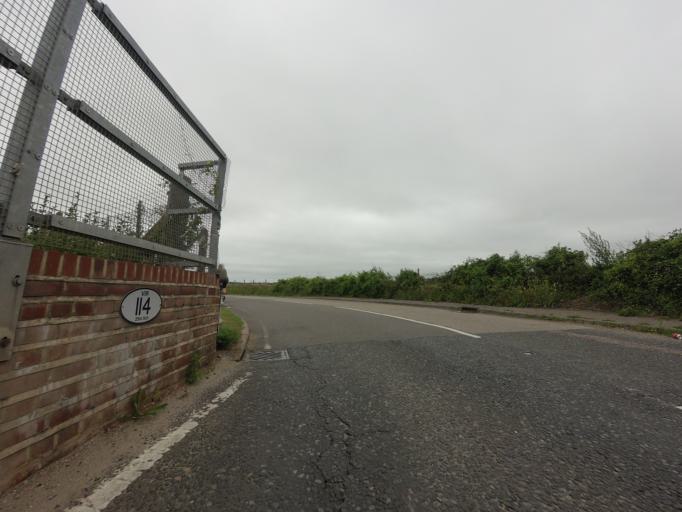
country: GB
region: England
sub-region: Kent
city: Meopham
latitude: 51.3865
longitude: 0.3367
